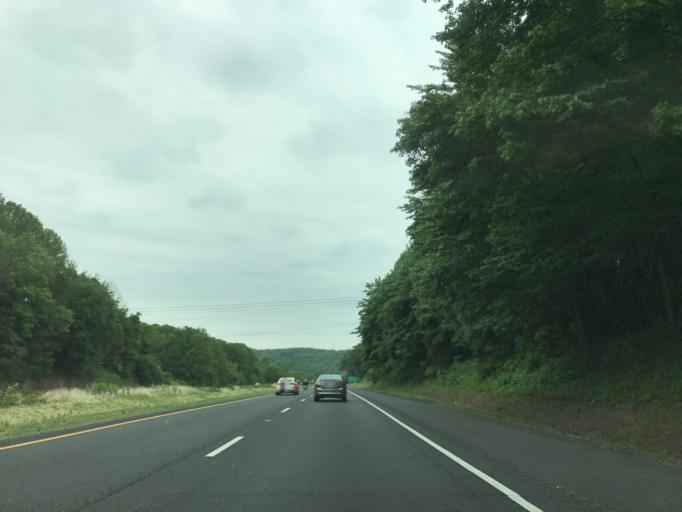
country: US
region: Pennsylvania
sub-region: York County
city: New Freedom
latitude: 39.6249
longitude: -76.6687
